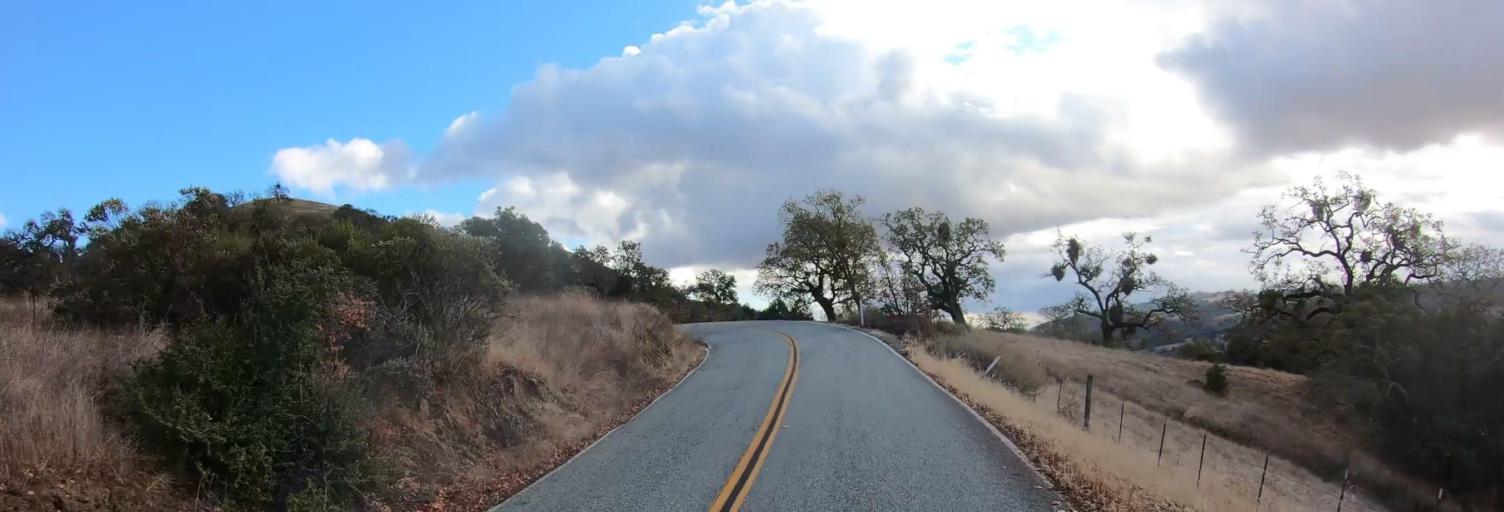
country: US
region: California
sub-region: Santa Clara County
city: East Foothills
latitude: 37.3347
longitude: -121.6992
